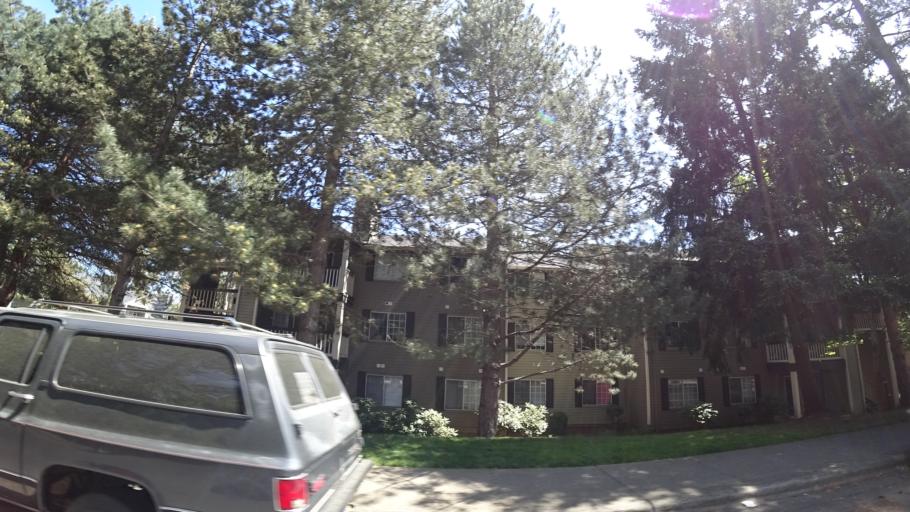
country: US
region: Oregon
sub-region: Washington County
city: Aloha
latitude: 45.4871
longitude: -122.8370
